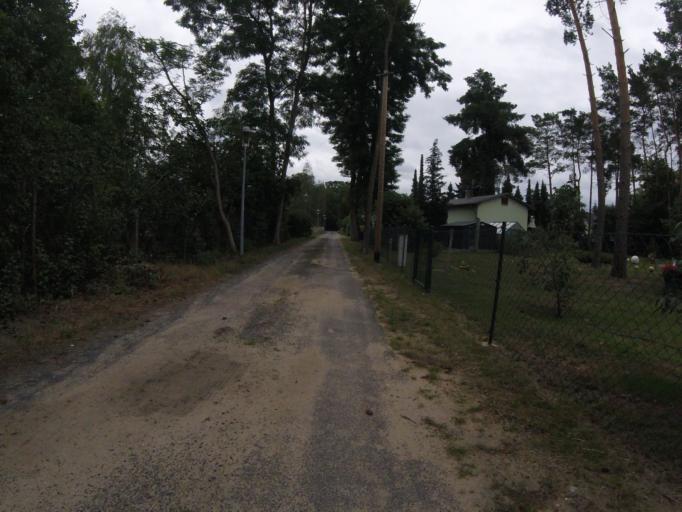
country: DE
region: Brandenburg
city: Mittenwalde
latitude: 52.2366
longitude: 13.5651
